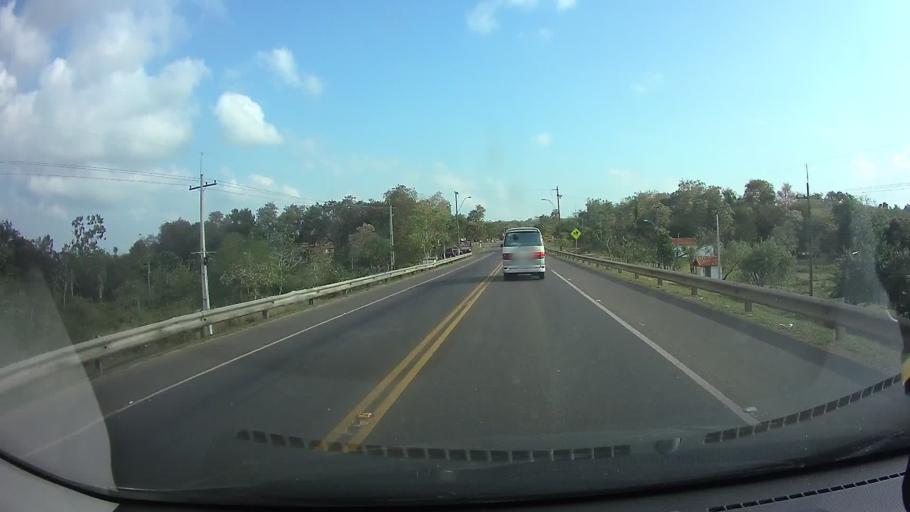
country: PY
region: Cordillera
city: Emboscada
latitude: -25.1118
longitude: -57.3123
